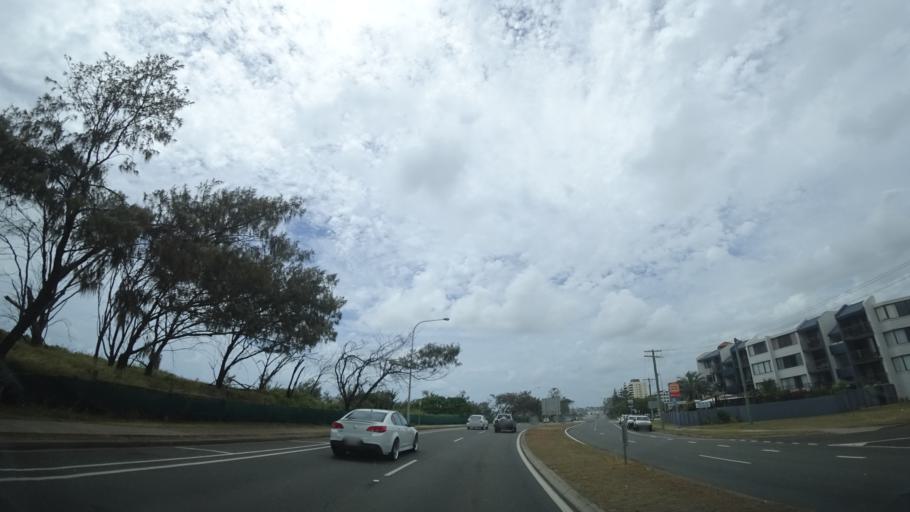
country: AU
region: Queensland
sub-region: Sunshine Coast
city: Mooloolaba
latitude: -26.6619
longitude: 153.1048
